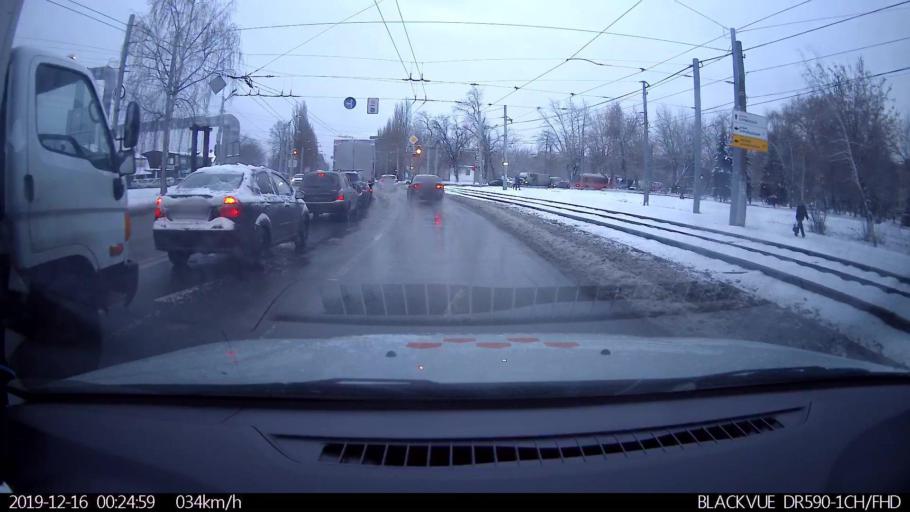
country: RU
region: Nizjnij Novgorod
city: Nizhniy Novgorod
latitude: 56.3366
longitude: 43.8856
